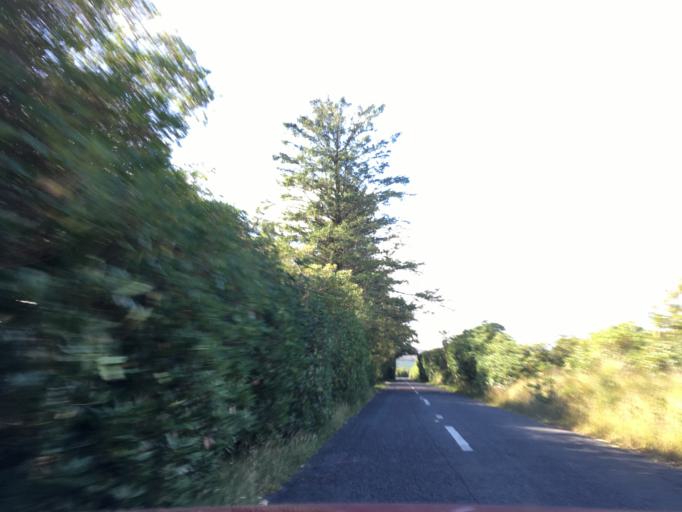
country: IE
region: Munster
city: Cahir
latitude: 52.2168
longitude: -7.9384
